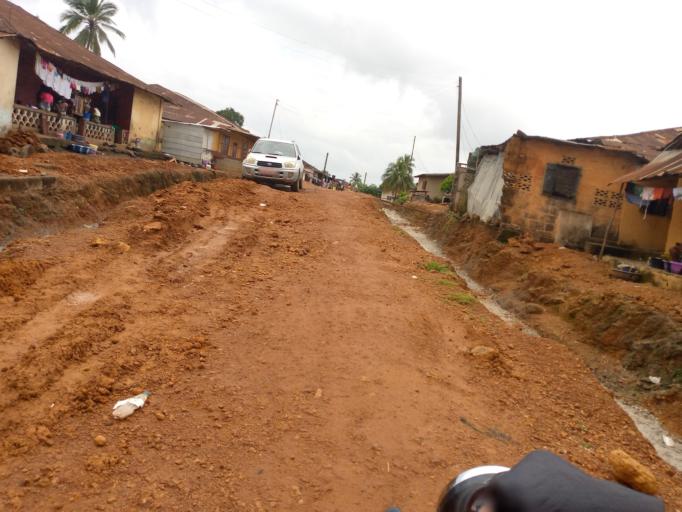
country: SL
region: Eastern Province
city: Kenema
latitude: 7.8743
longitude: -11.1874
